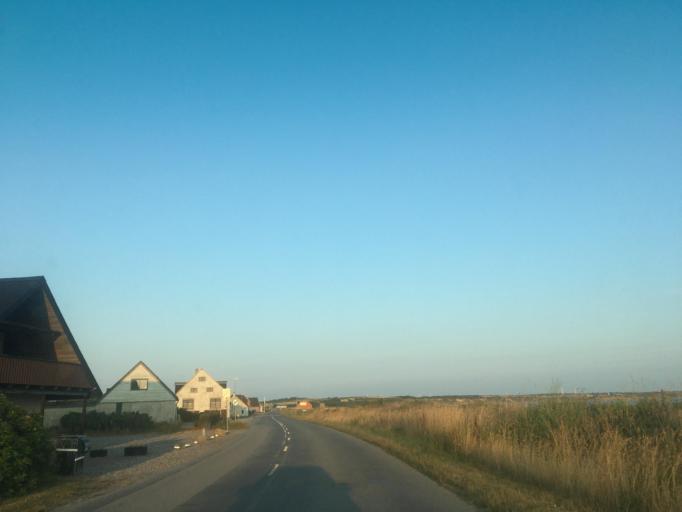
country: DK
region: Central Jutland
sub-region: Lemvig Kommune
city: Thyboron
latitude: 56.7716
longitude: 8.2750
